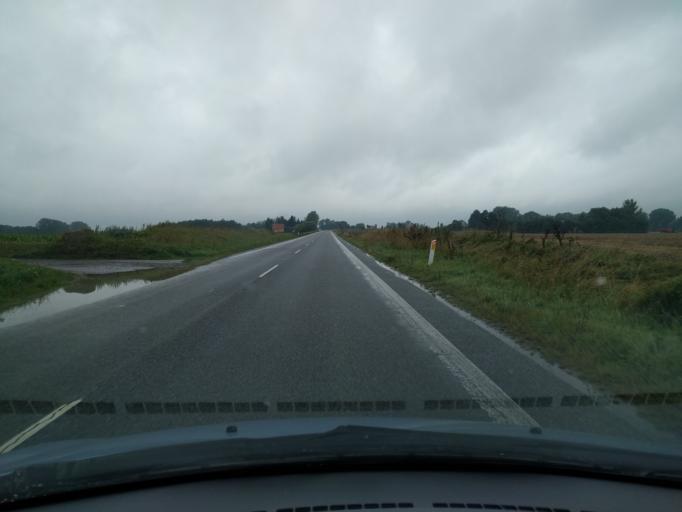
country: DK
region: Zealand
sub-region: Guldborgsund Kommune
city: Stubbekobing
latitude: 54.8918
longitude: 12.0079
